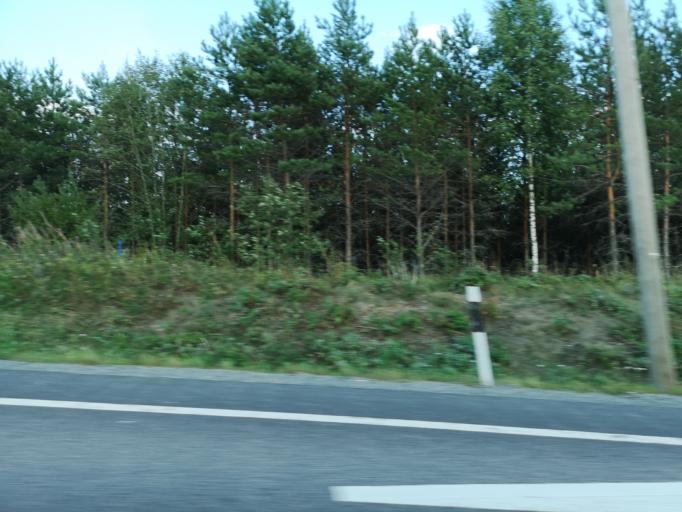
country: FI
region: Paijanne Tavastia
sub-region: Lahti
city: Hartola
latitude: 61.5448
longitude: 26.0080
